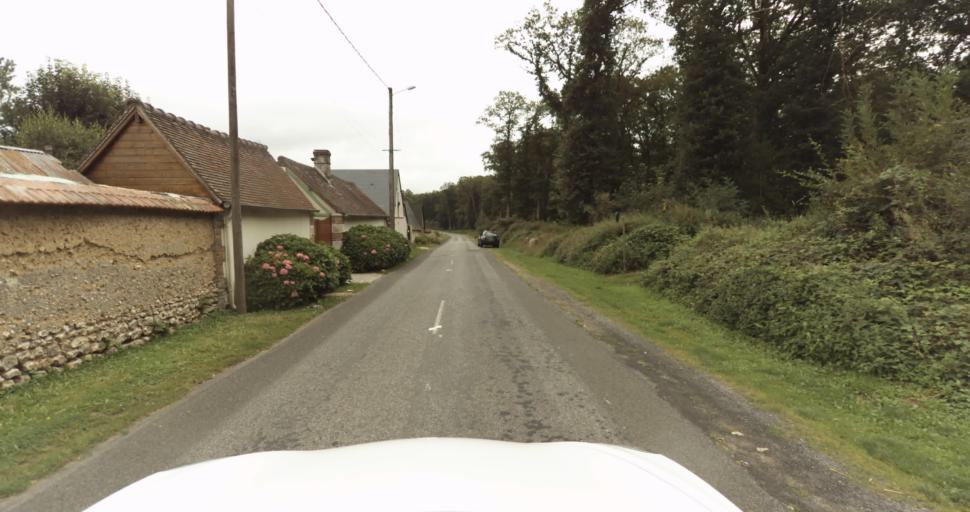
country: FR
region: Haute-Normandie
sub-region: Departement de l'Eure
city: Arnieres-sur-Iton
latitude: 48.9534
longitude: 1.0678
